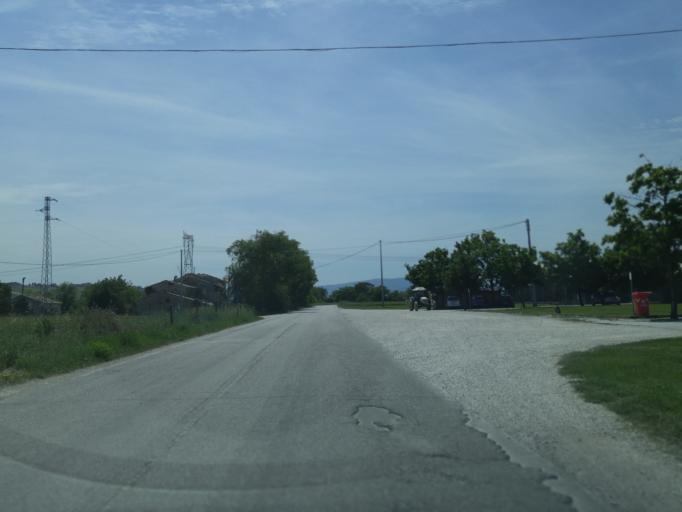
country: IT
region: The Marches
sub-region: Provincia di Pesaro e Urbino
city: Cuccurano
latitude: 43.7761
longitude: 12.9797
